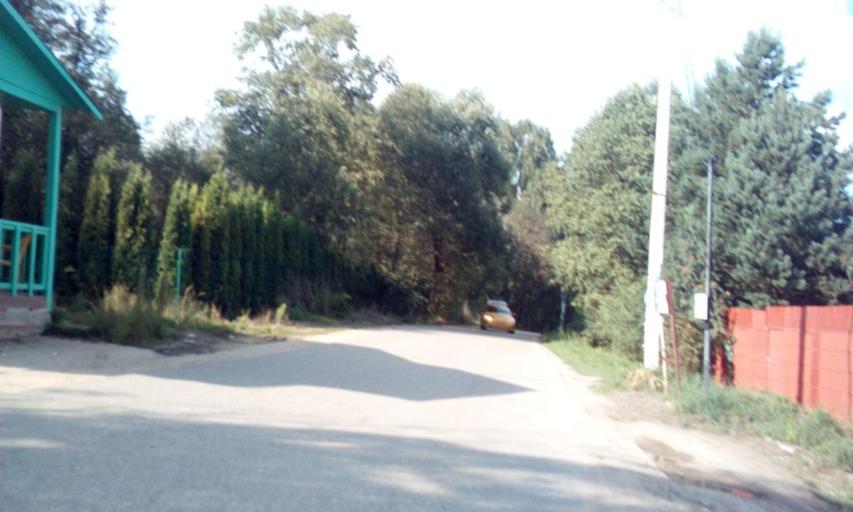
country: RU
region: Moskovskaya
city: Kolyubakino
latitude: 55.6414
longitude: 36.5634
